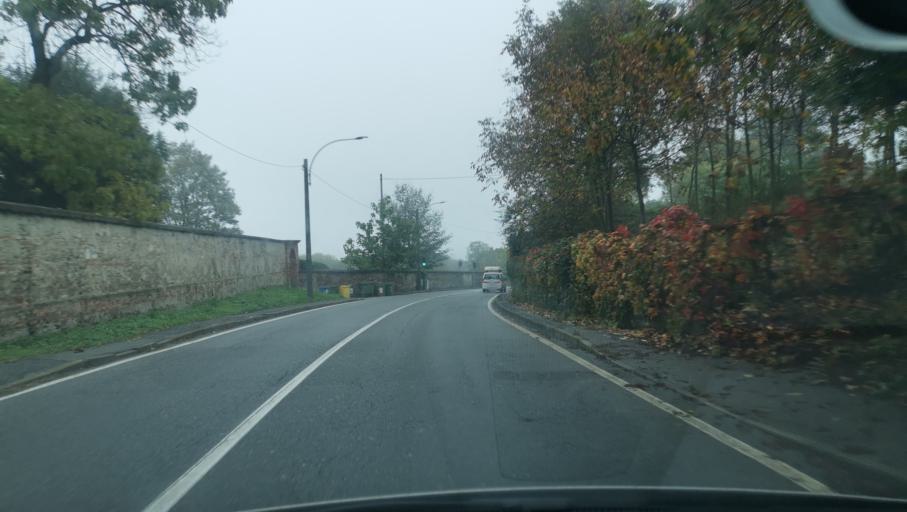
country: IT
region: Piedmont
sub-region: Provincia di Torino
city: San Mauro Torinese
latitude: 45.1155
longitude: 7.7823
